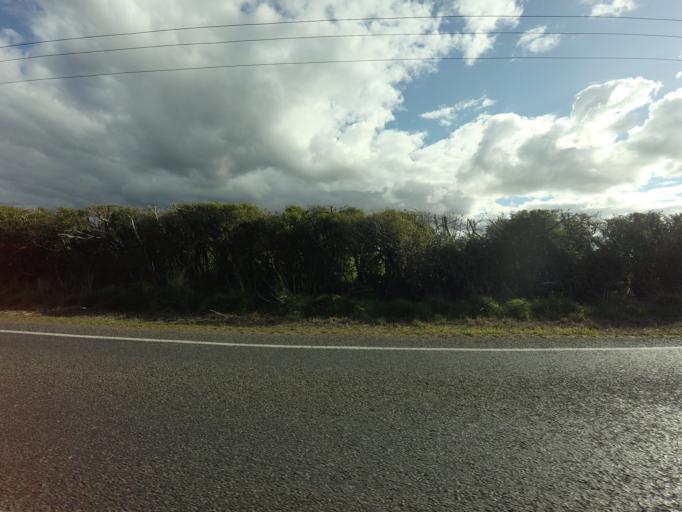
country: AU
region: Tasmania
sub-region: Northern Midlands
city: Longford
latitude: -41.7034
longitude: 147.0773
